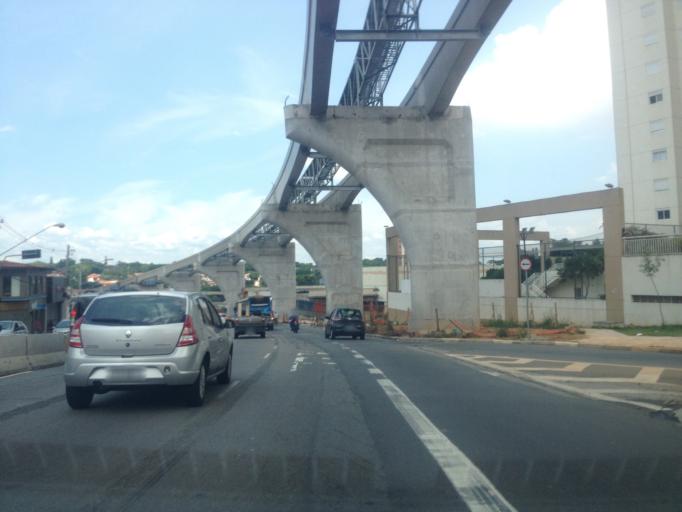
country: BR
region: Sao Paulo
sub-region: Diadema
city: Diadema
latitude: -23.6296
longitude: -46.6677
